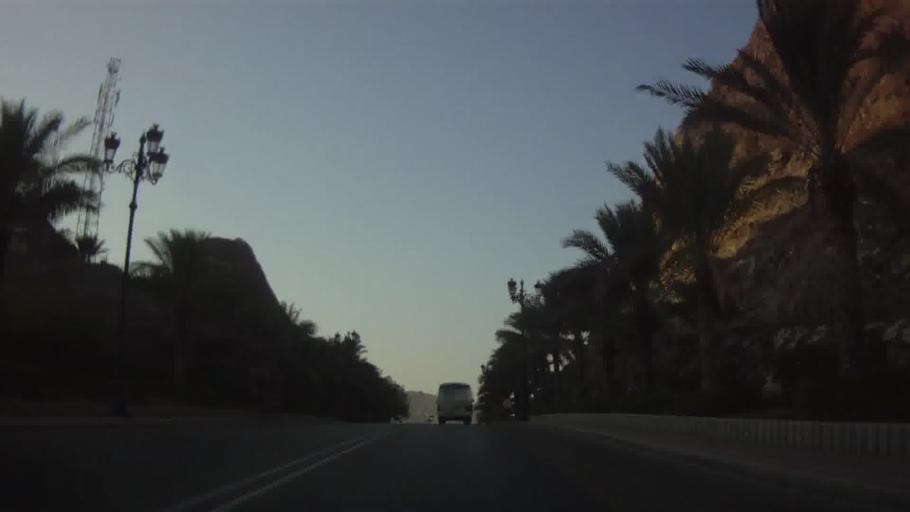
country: OM
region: Muhafazat Masqat
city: Muscat
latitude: 23.6072
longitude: 58.5968
